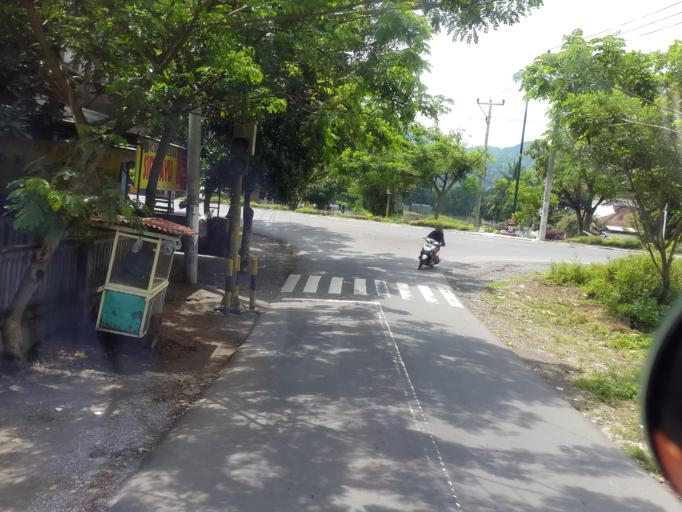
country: ID
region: West Nusa Tenggara
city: Karang Kuripan
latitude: -8.6662
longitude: 116.1599
